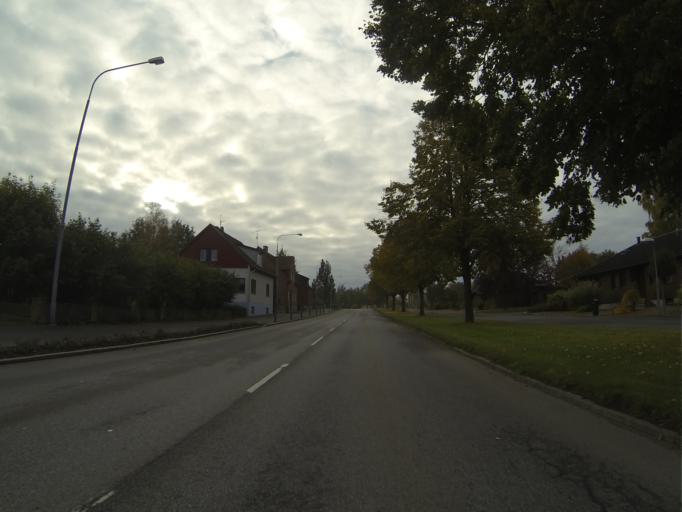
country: SE
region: Skane
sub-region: Tomelilla Kommun
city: Tomelilla
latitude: 55.5426
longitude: 13.9436
